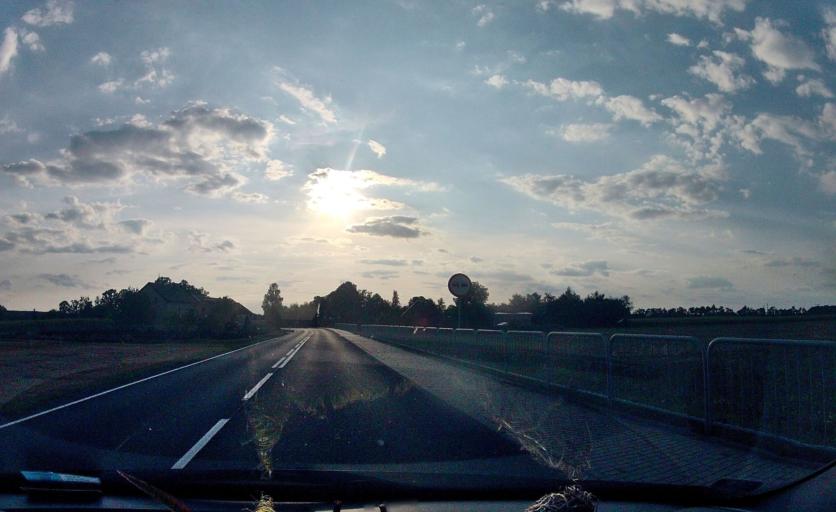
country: PL
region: Opole Voivodeship
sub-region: Powiat oleski
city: Gorzow Slaski
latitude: 51.0022
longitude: 18.3213
